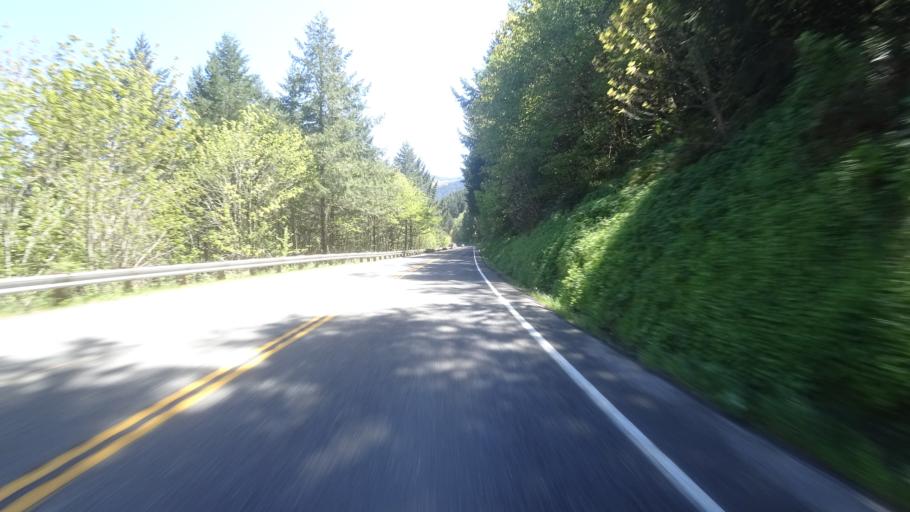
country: US
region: California
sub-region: Humboldt County
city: Blue Lake
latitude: 40.9055
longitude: -123.8218
